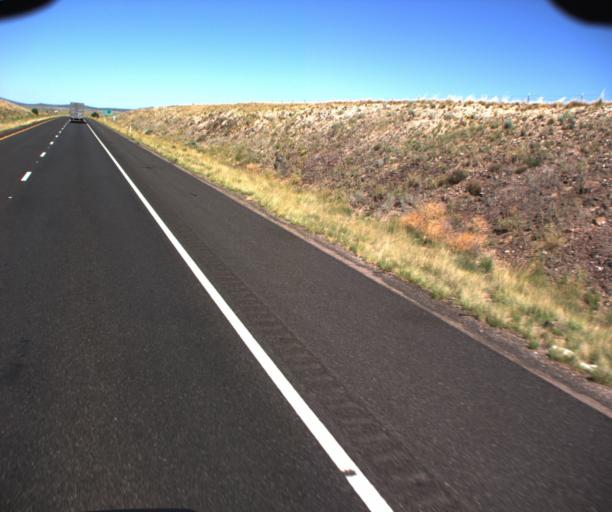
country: US
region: Arizona
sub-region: Yavapai County
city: Paulden
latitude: 35.2315
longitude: -112.5987
